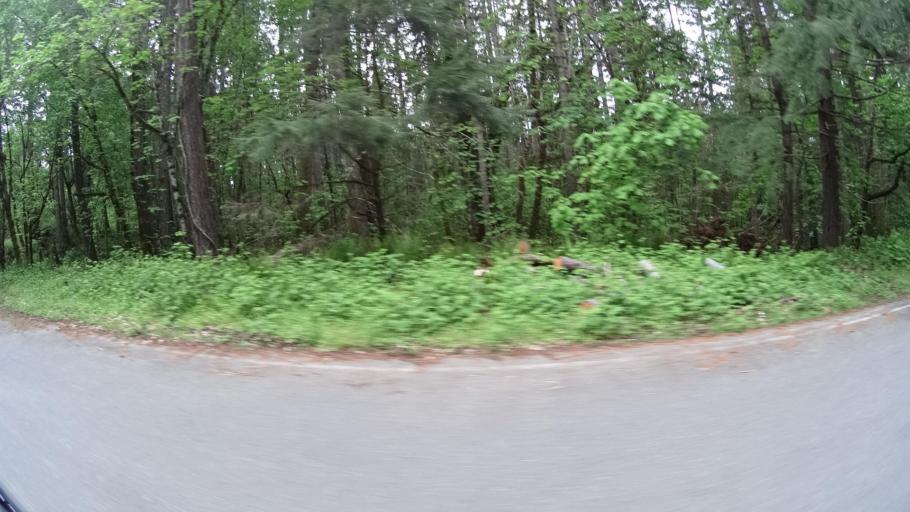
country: US
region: California
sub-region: Humboldt County
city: Willow Creek
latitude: 41.1195
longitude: -123.7274
